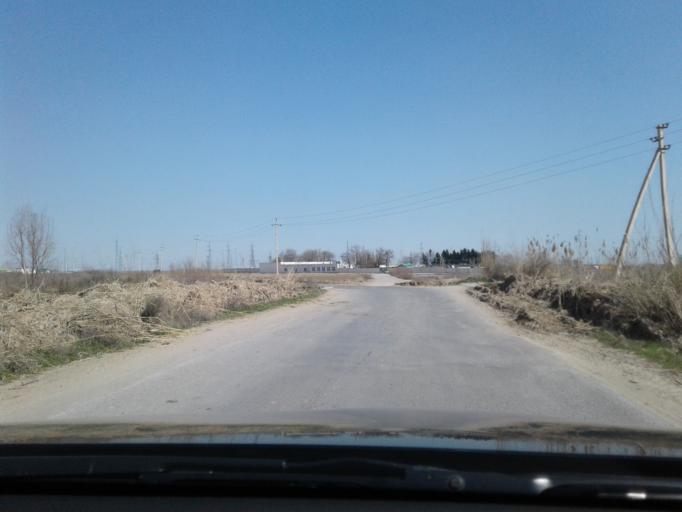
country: TM
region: Ahal
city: Abadan
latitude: 38.1012
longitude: 58.2042
